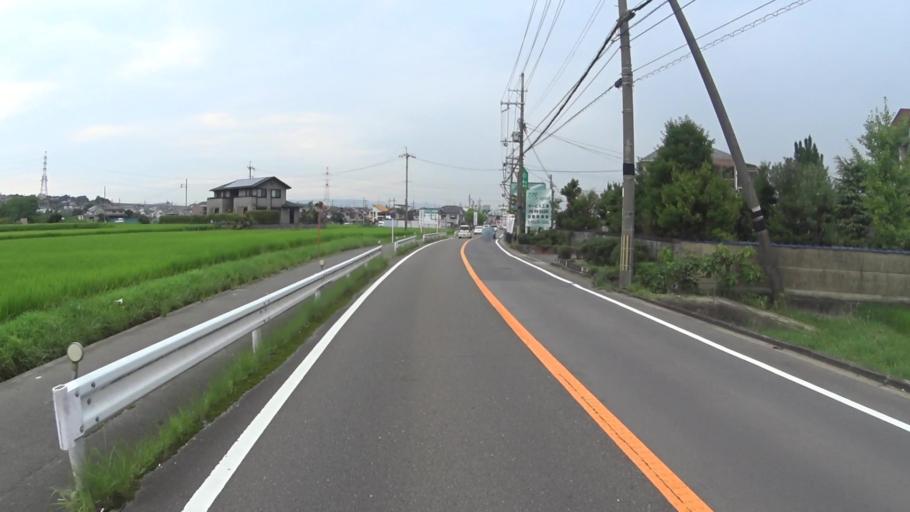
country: JP
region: Kyoto
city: Tanabe
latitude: 34.8001
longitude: 135.7830
